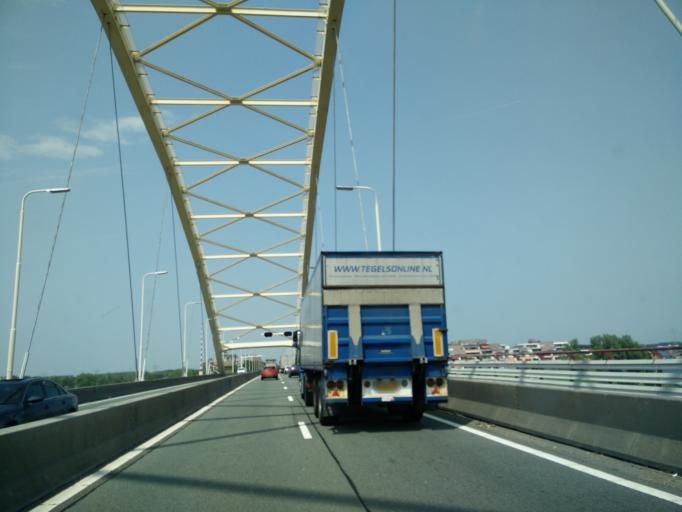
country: NL
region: South Holland
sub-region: Gemeente Papendrecht
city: Papendrecht
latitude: 51.8228
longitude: 4.7059
